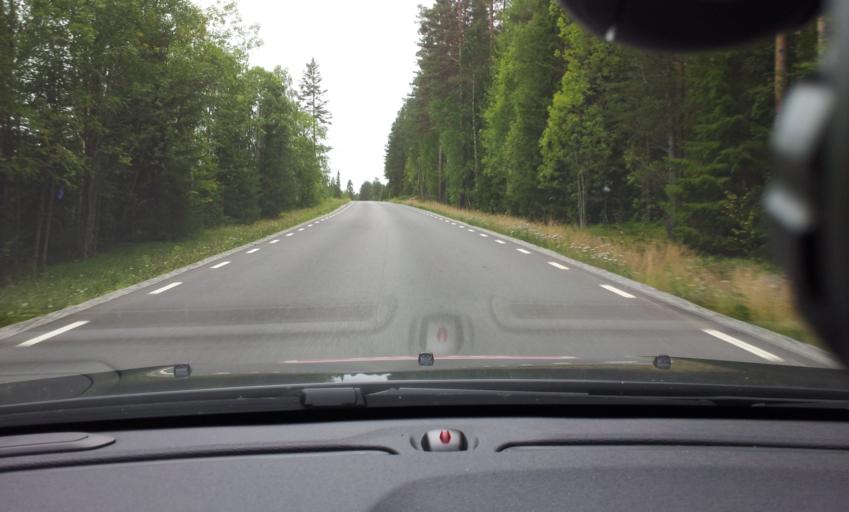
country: SE
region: Jaemtland
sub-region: Braecke Kommun
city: Braecke
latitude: 63.1256
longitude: 15.4982
